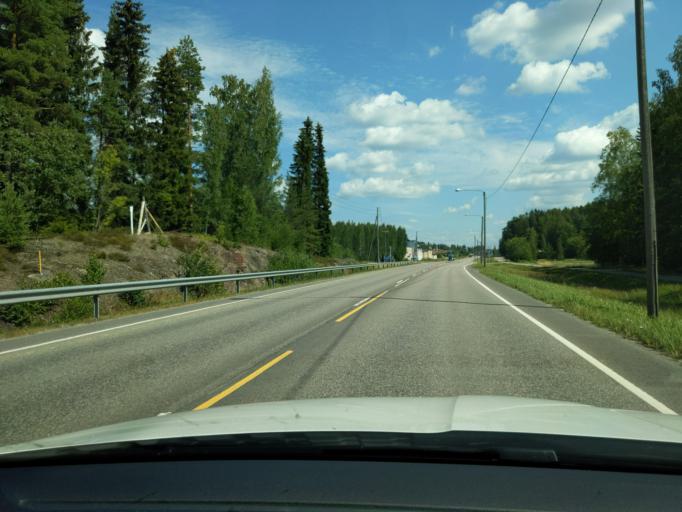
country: FI
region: Uusimaa
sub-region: Helsinki
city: Maentsaelae
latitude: 60.6206
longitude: 25.2828
